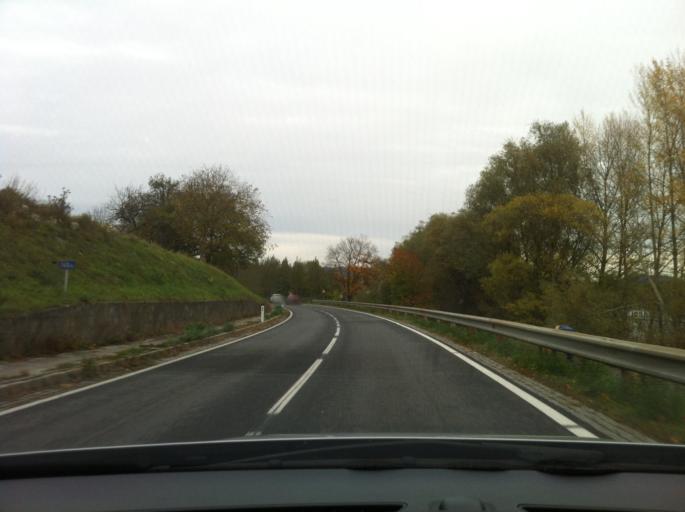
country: AT
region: Lower Austria
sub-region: Politischer Bezirk Melk
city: Melk
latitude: 48.2333
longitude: 15.3202
